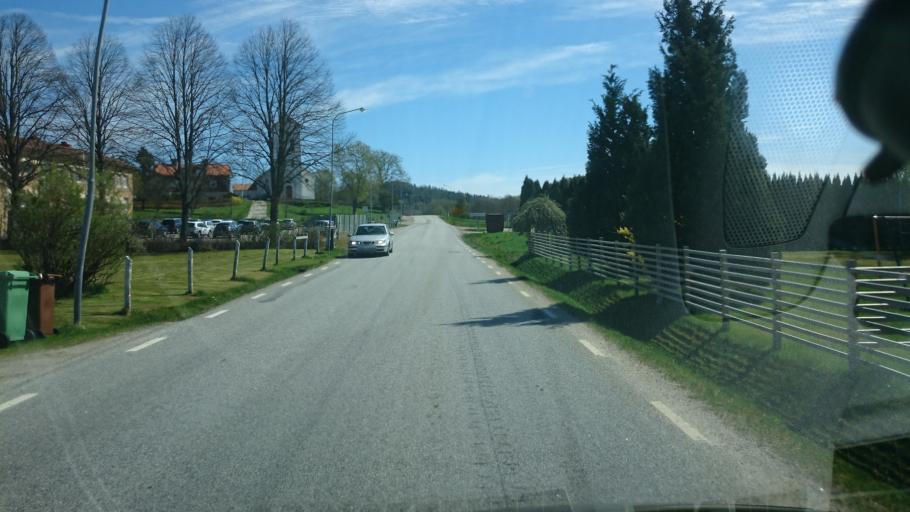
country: SE
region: Vaestra Goetaland
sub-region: Munkedals Kommun
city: Munkedal
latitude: 58.3803
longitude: 11.6676
